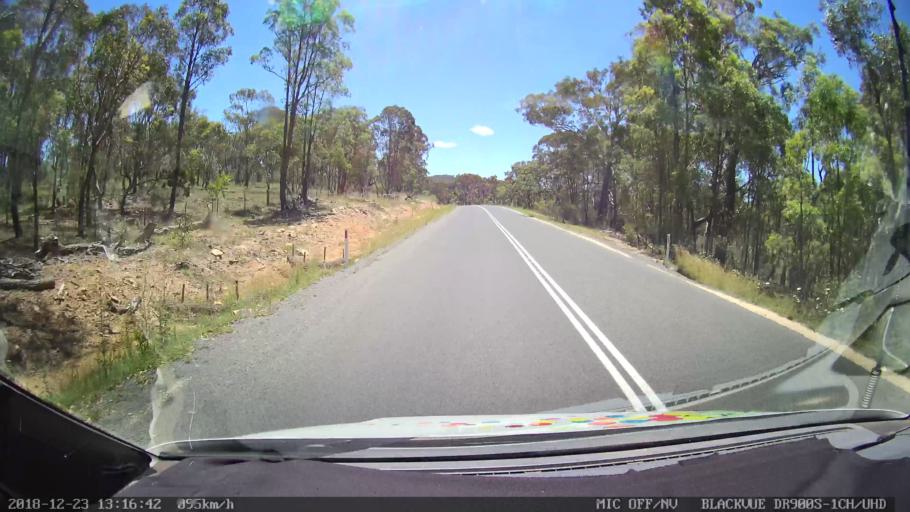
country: AU
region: New South Wales
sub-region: Armidale Dumaresq
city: Armidale
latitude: -30.4971
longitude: 151.4976
